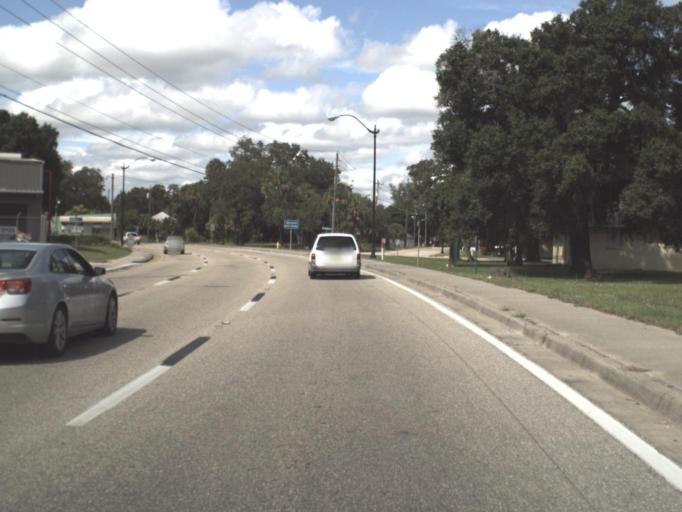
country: US
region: Florida
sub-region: Lee County
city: Fort Myers
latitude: 26.6442
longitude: -81.8603
